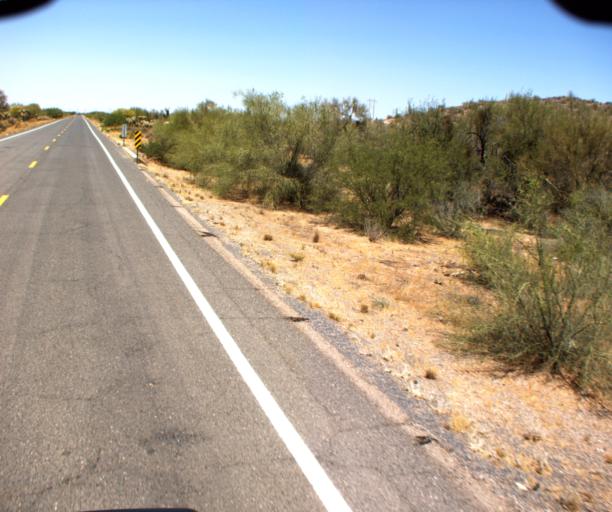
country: US
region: Arizona
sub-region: Pinal County
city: Florence
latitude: 32.7822
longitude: -111.1676
